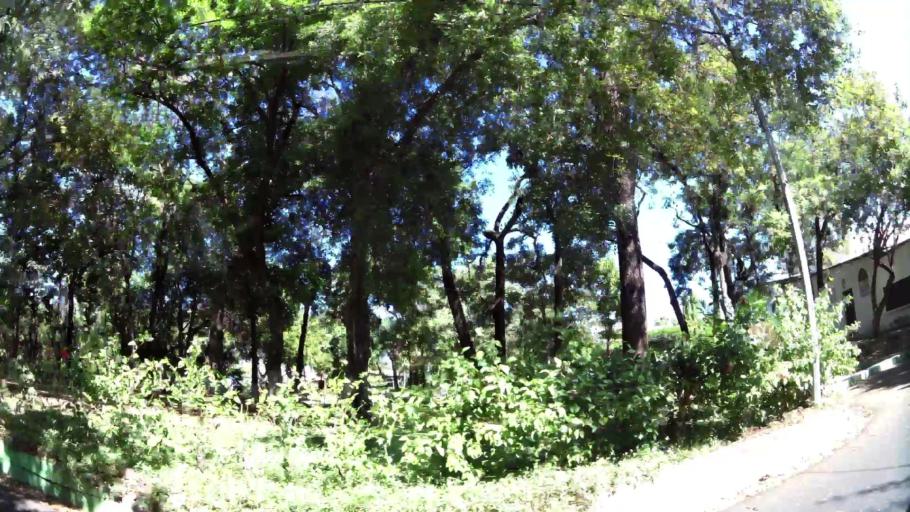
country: SV
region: San Miguel
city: San Miguel
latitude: 13.4766
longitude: -88.1685
